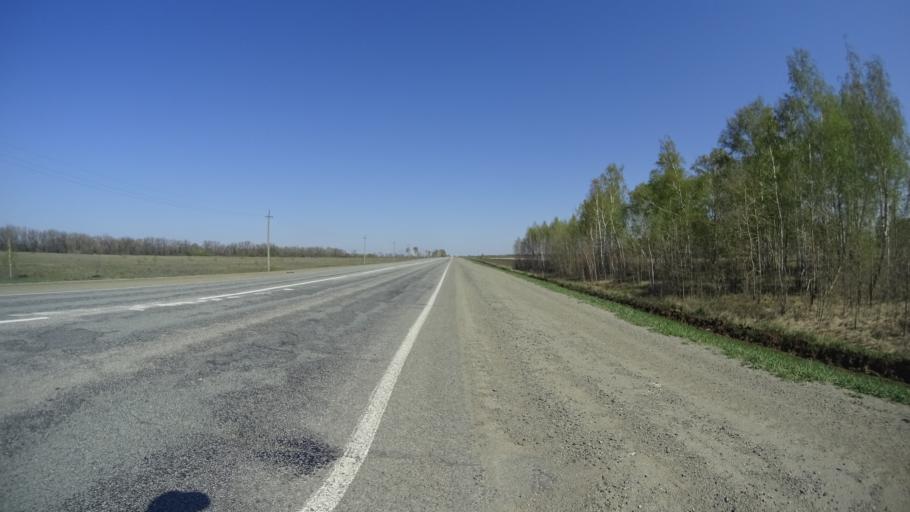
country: RU
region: Chelyabinsk
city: Troitsk
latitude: 54.1900
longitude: 61.4336
